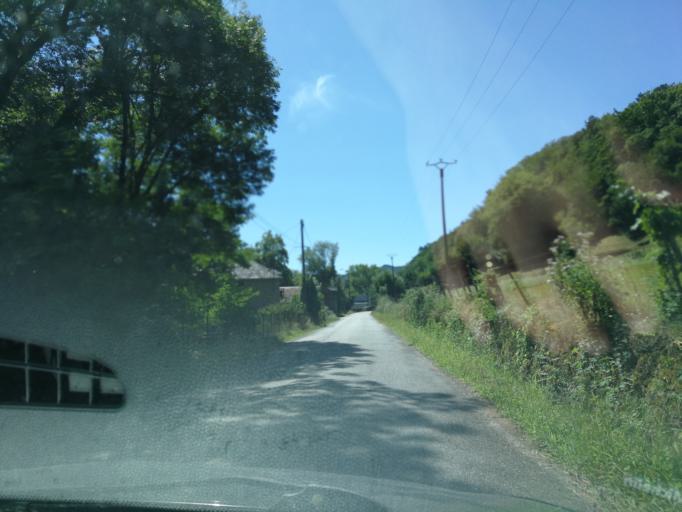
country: FR
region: Limousin
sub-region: Departement de la Correze
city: Argentat
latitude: 45.0913
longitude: 1.9257
